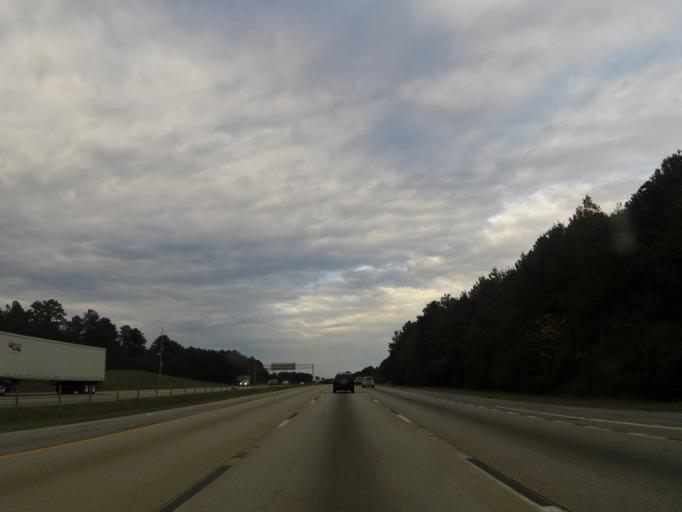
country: US
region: Alabama
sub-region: Jefferson County
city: Hoover
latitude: 33.4032
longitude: -86.7696
